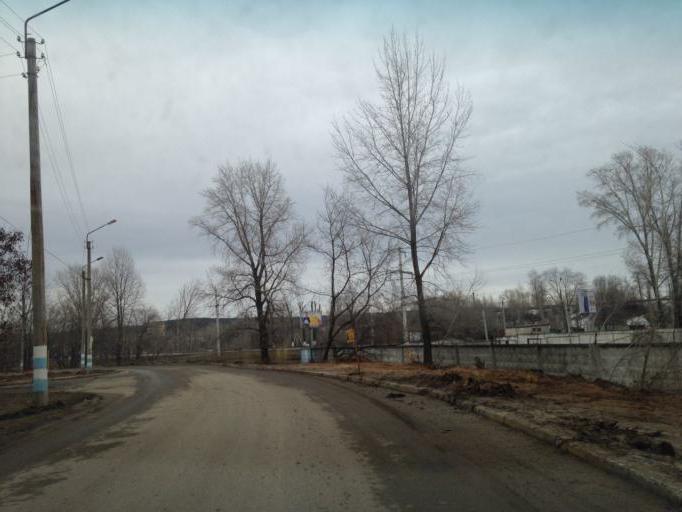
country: RU
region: Ulyanovsk
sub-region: Ulyanovskiy Rayon
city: Ulyanovsk
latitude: 54.3208
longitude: 48.4711
